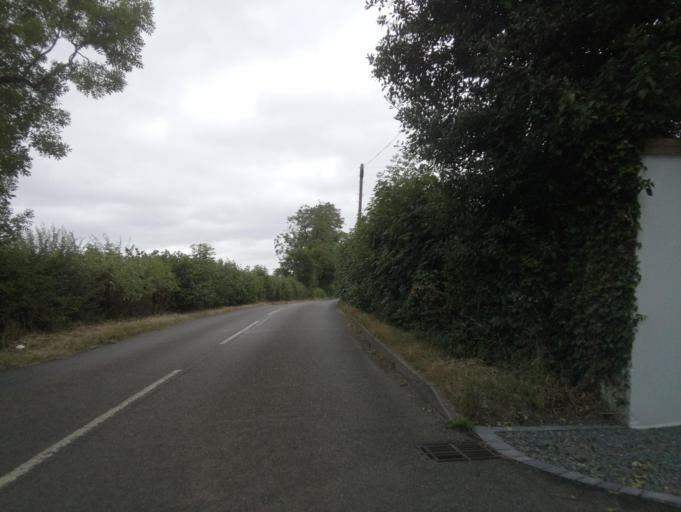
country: GB
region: England
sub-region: Leicestershire
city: Ashby de la Zouch
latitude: 52.7380
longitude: -1.4878
